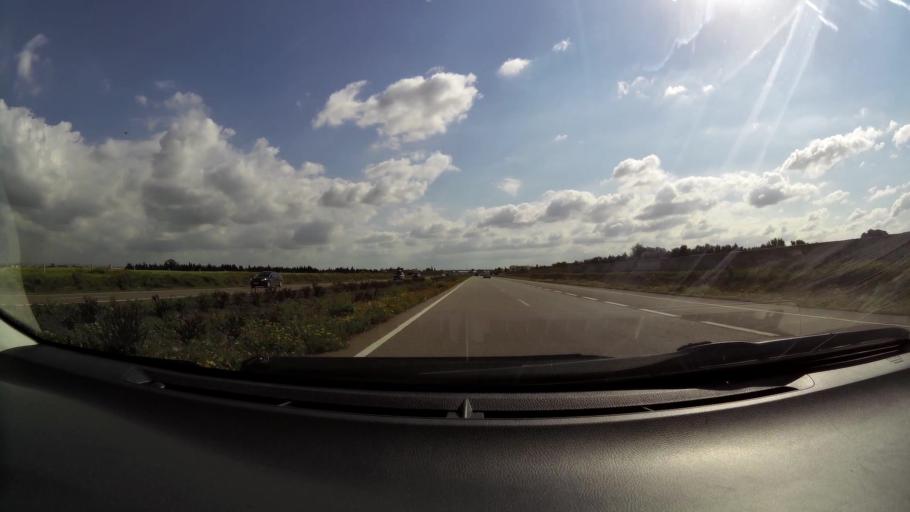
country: MA
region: Chaouia-Ouardigha
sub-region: Settat Province
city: Berrechid
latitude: 33.2649
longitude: -7.5523
